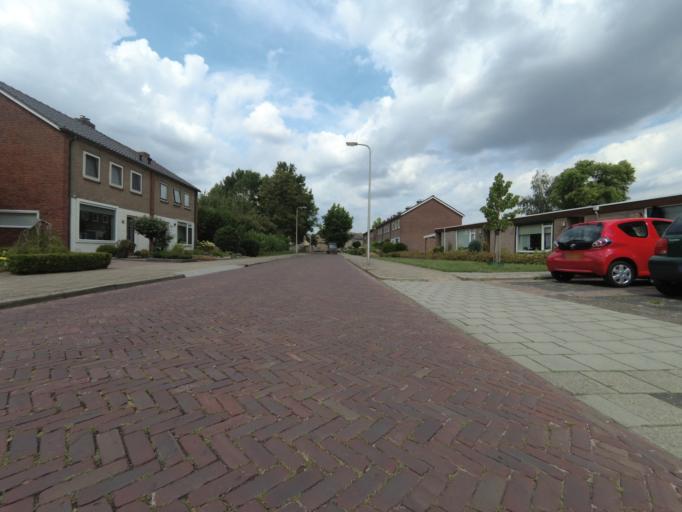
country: NL
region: Overijssel
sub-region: Gemeente Haaksbergen
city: Haaksbergen
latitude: 52.1579
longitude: 6.7441
